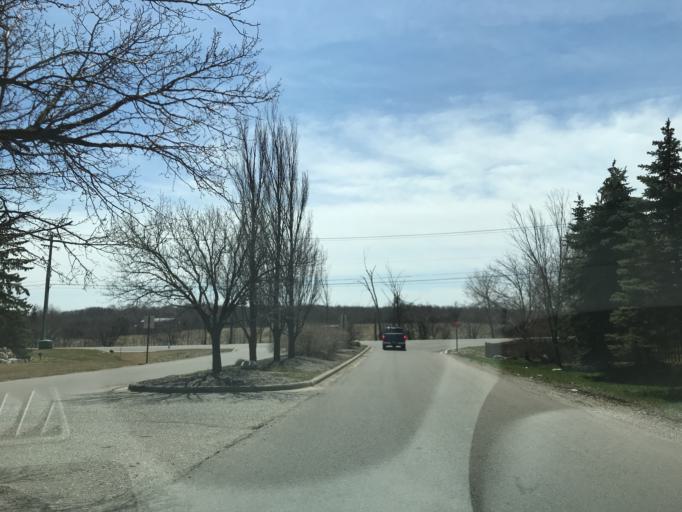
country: US
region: Michigan
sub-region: Washtenaw County
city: Ann Arbor
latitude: 42.2567
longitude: -83.7872
